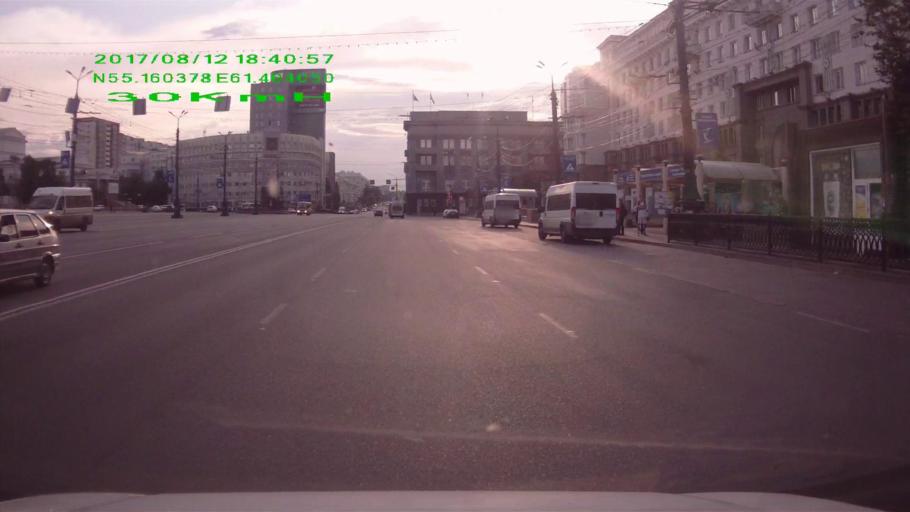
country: RU
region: Chelyabinsk
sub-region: Gorod Chelyabinsk
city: Chelyabinsk
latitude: 55.1591
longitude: 61.3994
